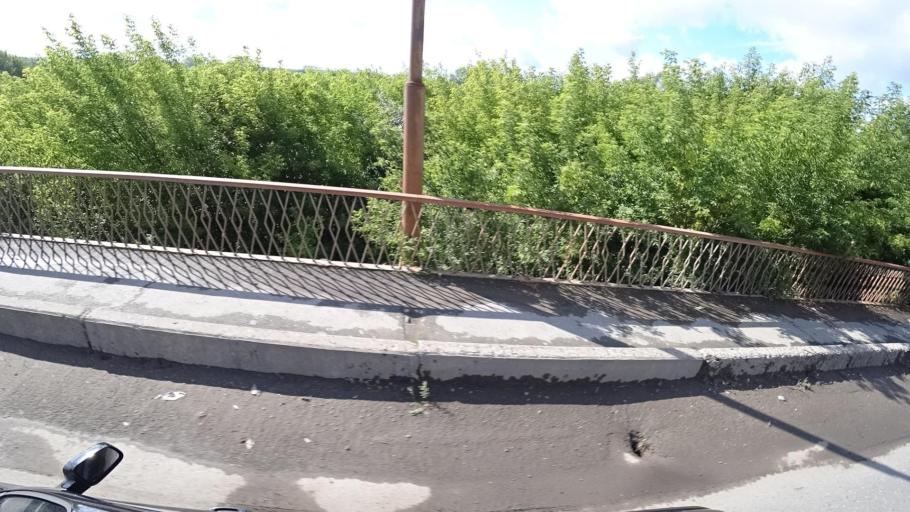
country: RU
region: Sverdlovsk
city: Kamyshlov
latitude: 56.8403
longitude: 62.7035
